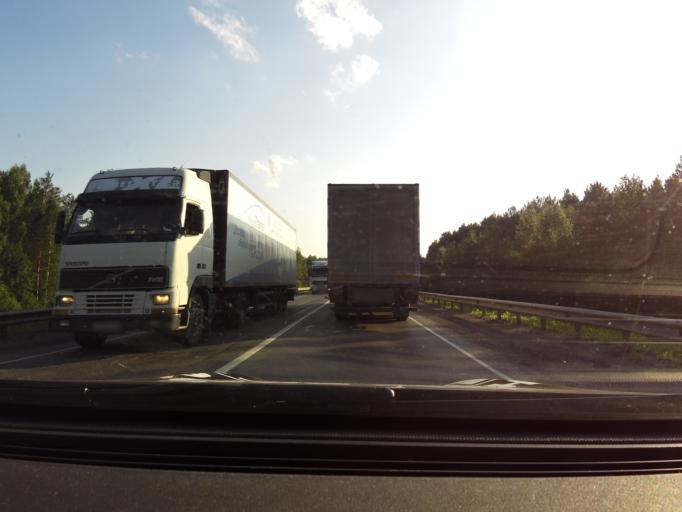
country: RU
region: Sverdlovsk
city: Druzhinino
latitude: 56.8033
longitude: 59.4781
